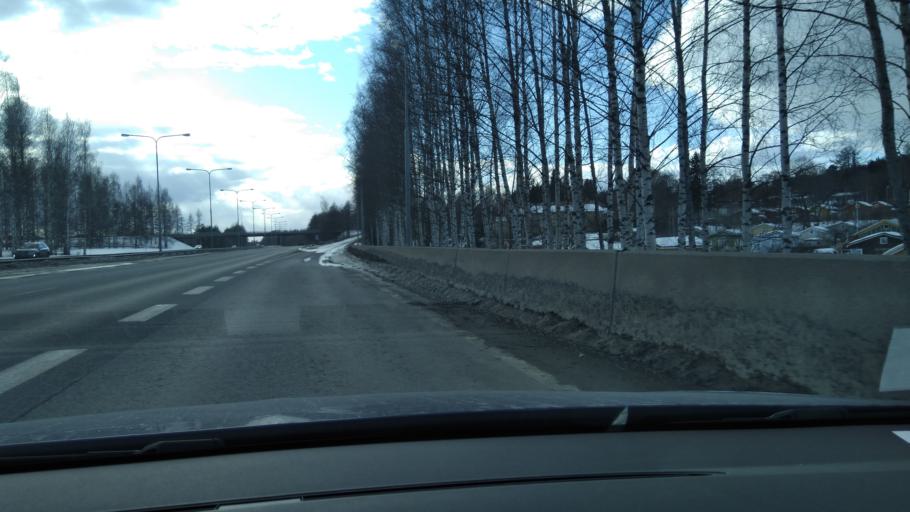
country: FI
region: Pirkanmaa
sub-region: Tampere
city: Pirkkala
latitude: 61.4985
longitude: 23.6604
